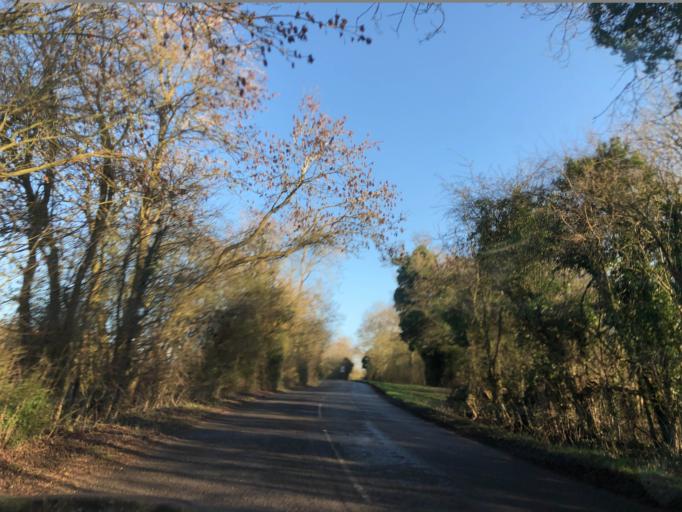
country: GB
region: England
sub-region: Warwickshire
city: Harbury
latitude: 52.2063
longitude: -1.5004
